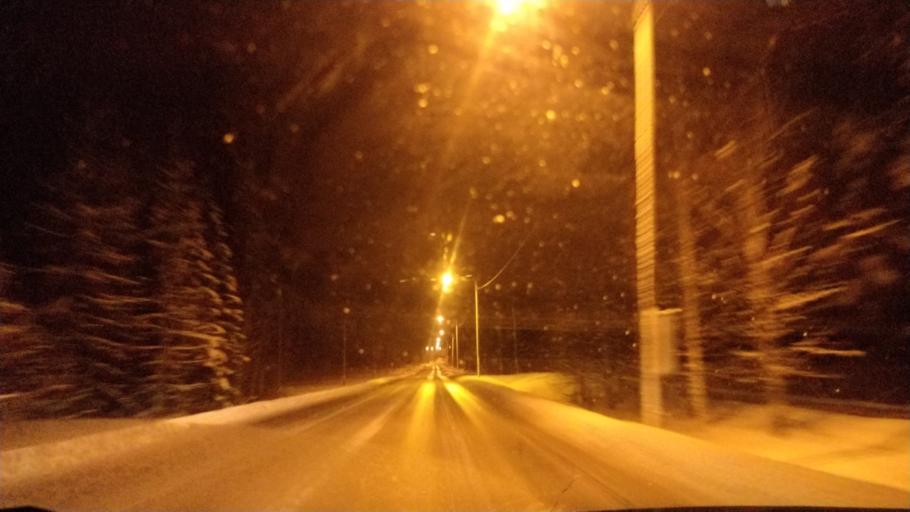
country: FI
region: Lapland
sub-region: Rovaniemi
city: Rovaniemi
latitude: 66.2959
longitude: 25.3517
